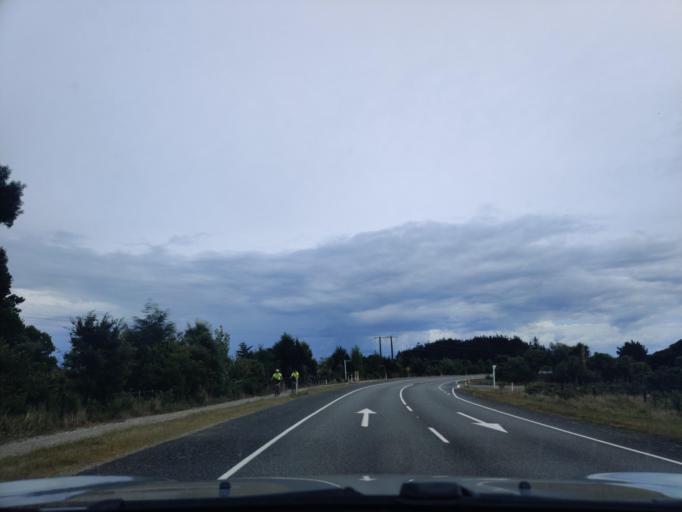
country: NZ
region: West Coast
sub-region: Westland District
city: Hokitika
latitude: -42.8105
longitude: 170.8877
